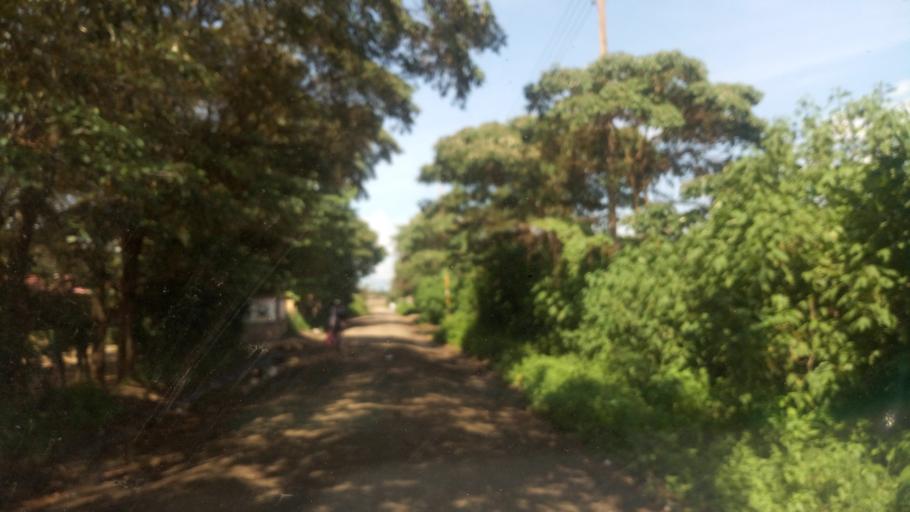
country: KE
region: Nakuru
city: Nakuru
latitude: -0.2773
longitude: 36.1151
